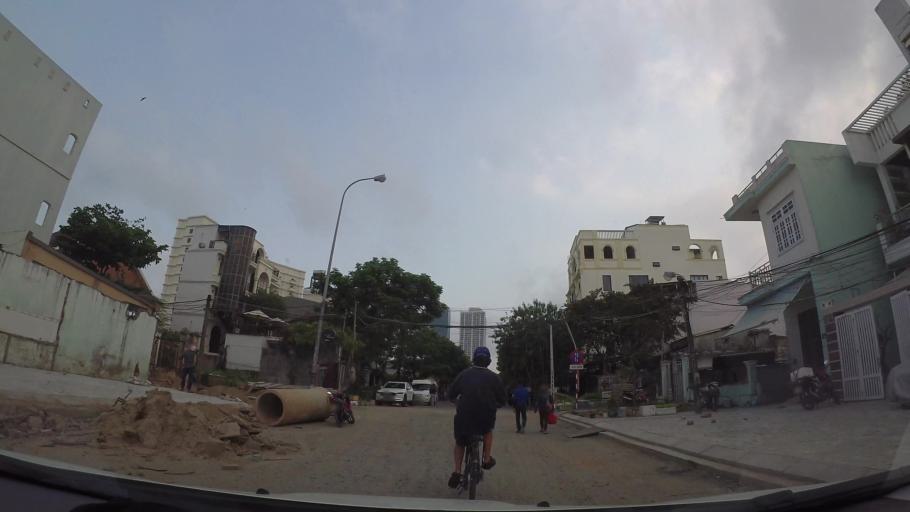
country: VN
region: Da Nang
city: Son Tra
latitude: 16.0589
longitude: 108.2447
